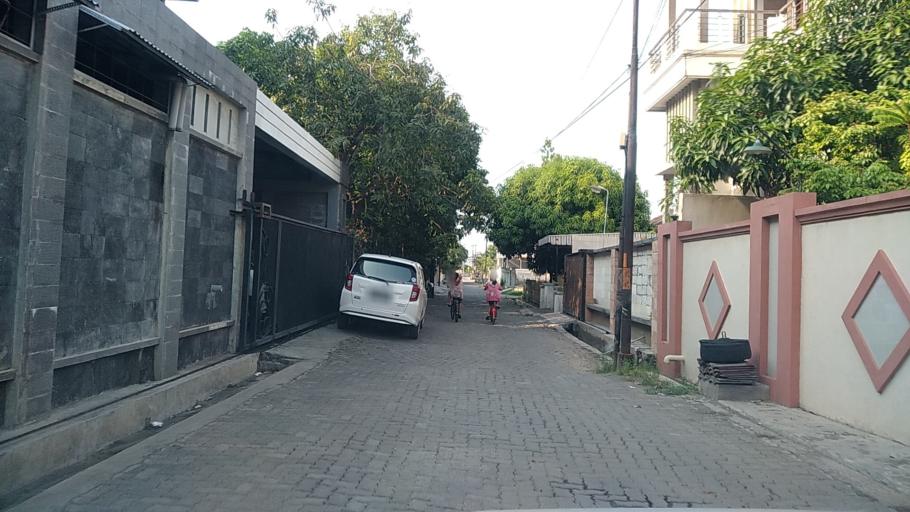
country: ID
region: Central Java
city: Semarang
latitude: -6.9556
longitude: 110.4072
